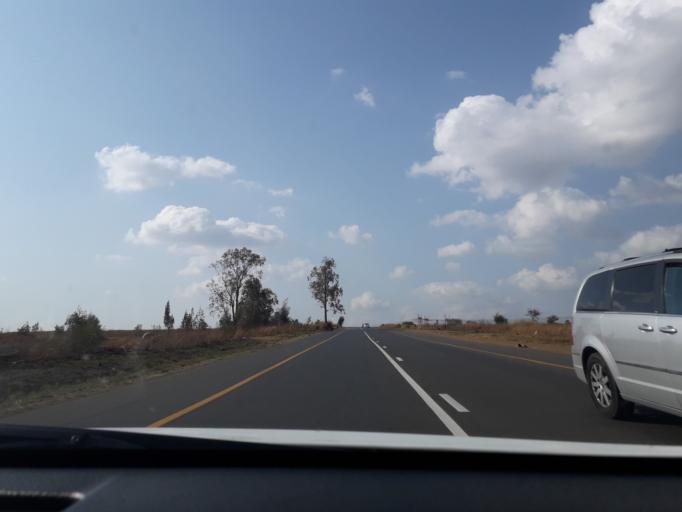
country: ZA
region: Gauteng
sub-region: Ekurhuleni Metropolitan Municipality
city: Tembisa
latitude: -25.9243
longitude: 28.2454
